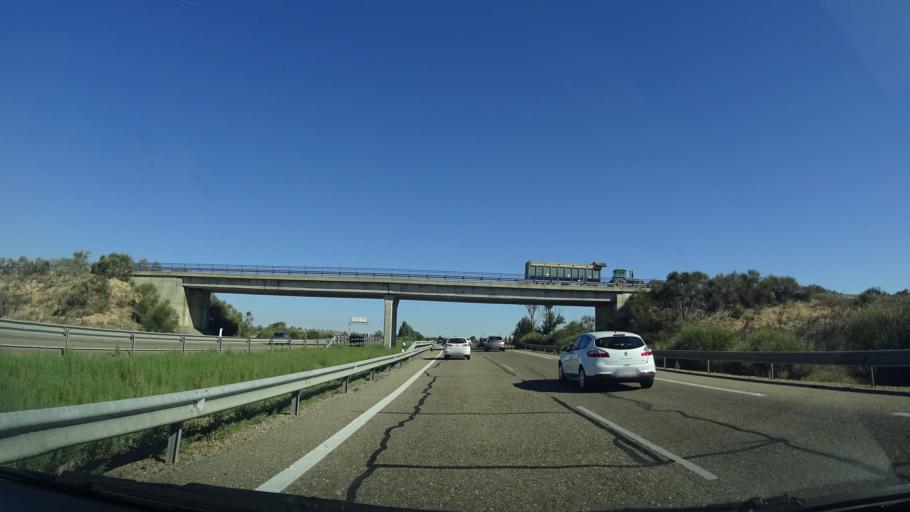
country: ES
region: Castille and Leon
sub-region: Provincia de Zamora
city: Villalpando
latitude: 41.8632
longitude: -5.4282
